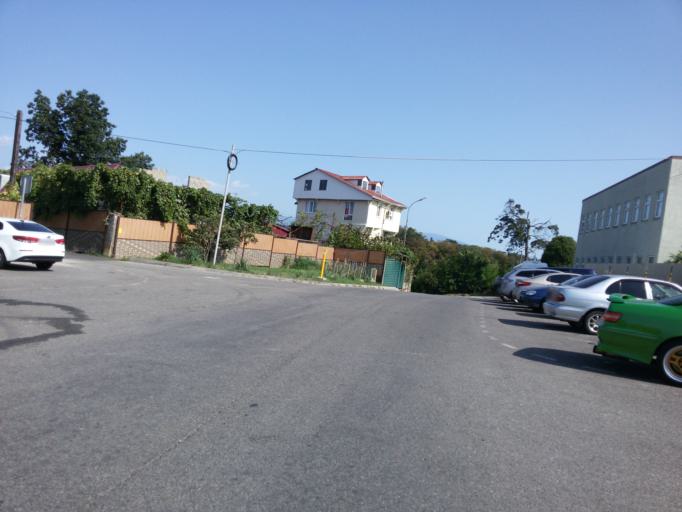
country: RU
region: Krasnodarskiy
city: Adler
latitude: 43.4186
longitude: 39.9388
